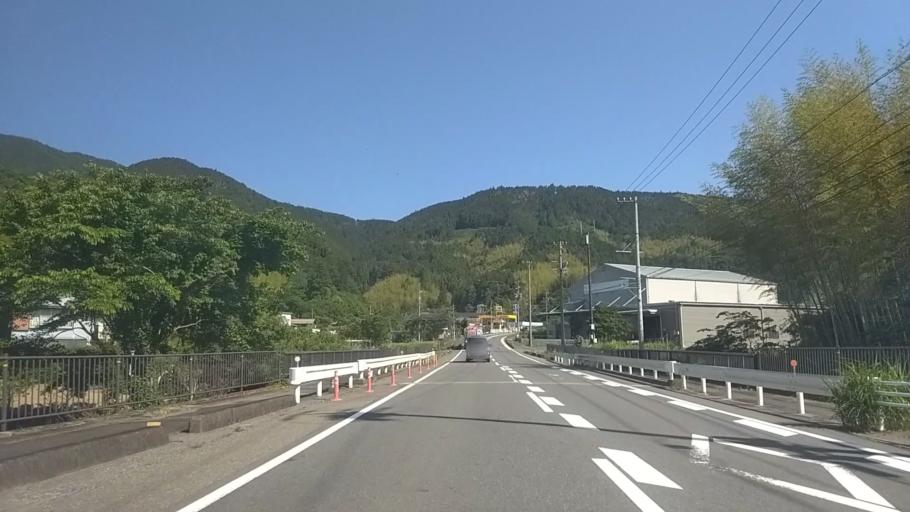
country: JP
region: Shizuoka
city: Fujinomiya
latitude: 35.1603
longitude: 138.5191
